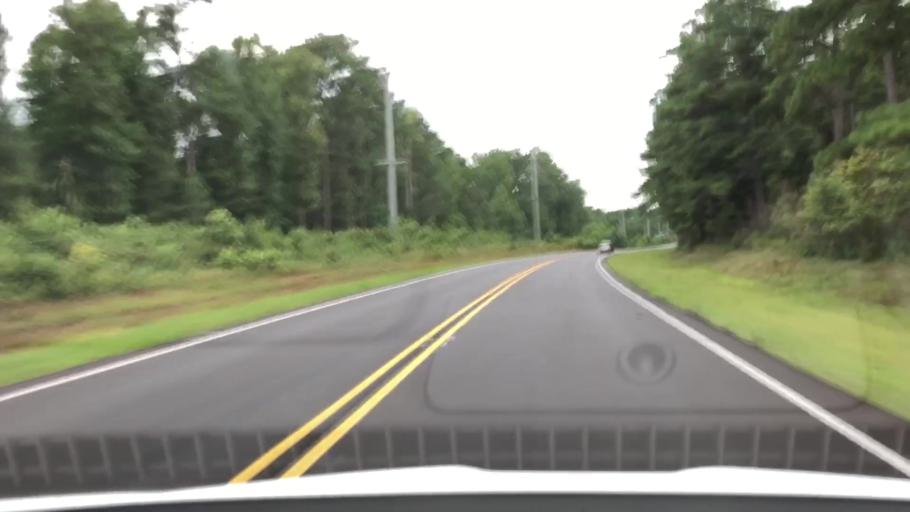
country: US
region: North Carolina
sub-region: Jones County
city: Maysville
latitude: 34.8245
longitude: -77.1530
